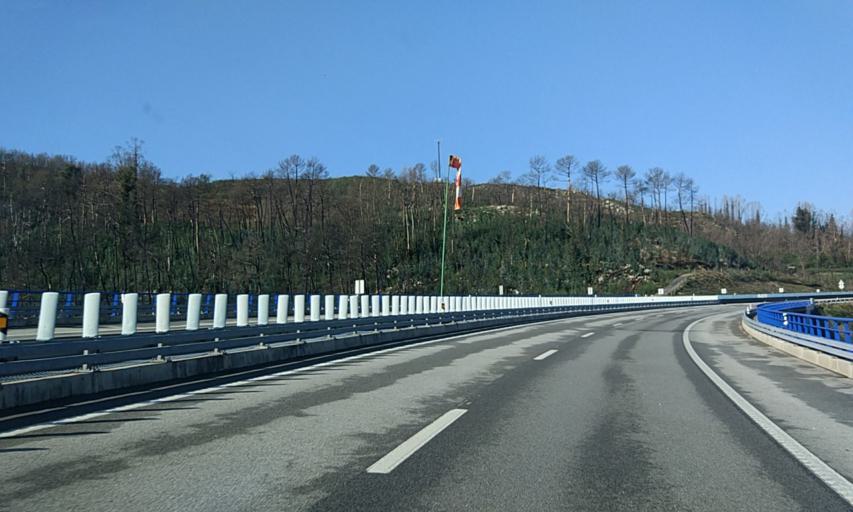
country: PT
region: Viseu
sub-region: Vouzela
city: Vouzela
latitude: 40.6973
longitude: -8.0986
